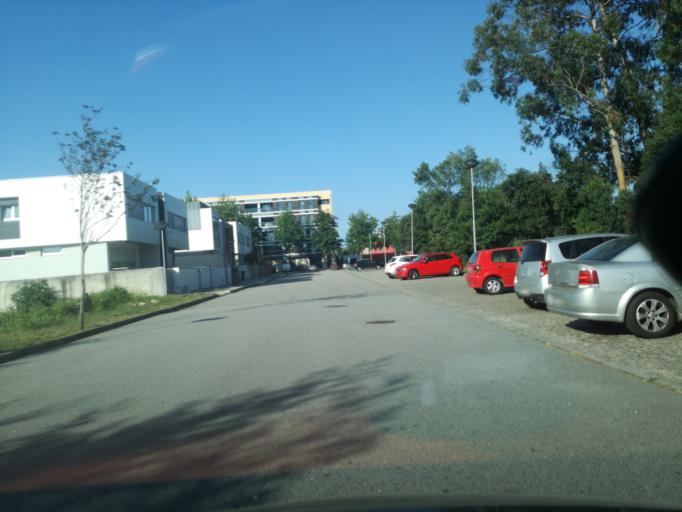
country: PT
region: Porto
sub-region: Maia
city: Gemunde
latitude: 41.2514
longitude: -8.6542
